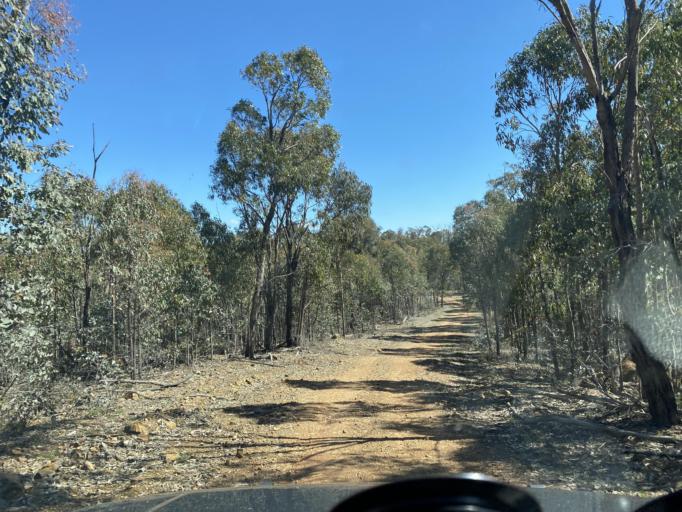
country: AU
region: Victoria
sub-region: Benalla
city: Benalla
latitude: -36.7265
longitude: 146.1824
